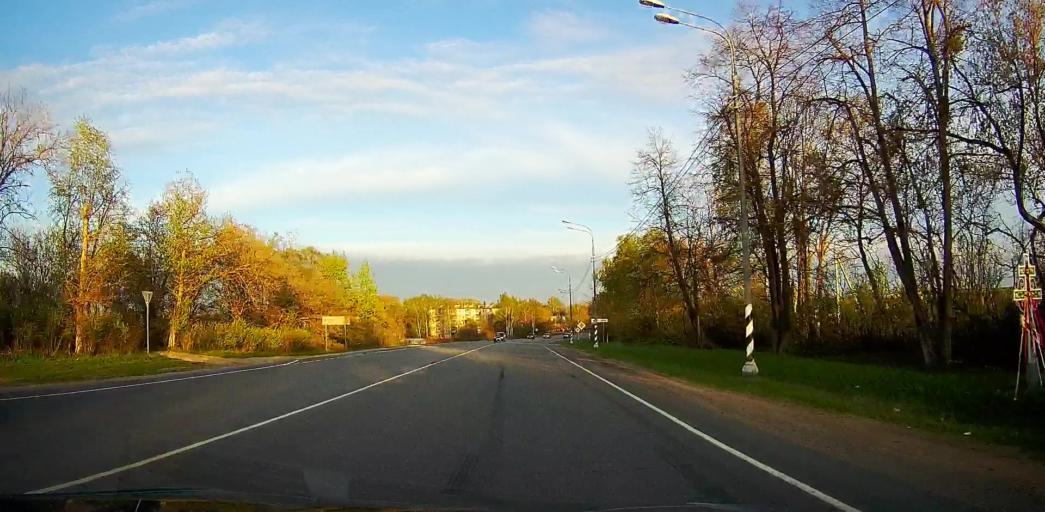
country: RU
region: Moskovskaya
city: Troitskoye
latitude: 55.2111
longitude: 38.6035
